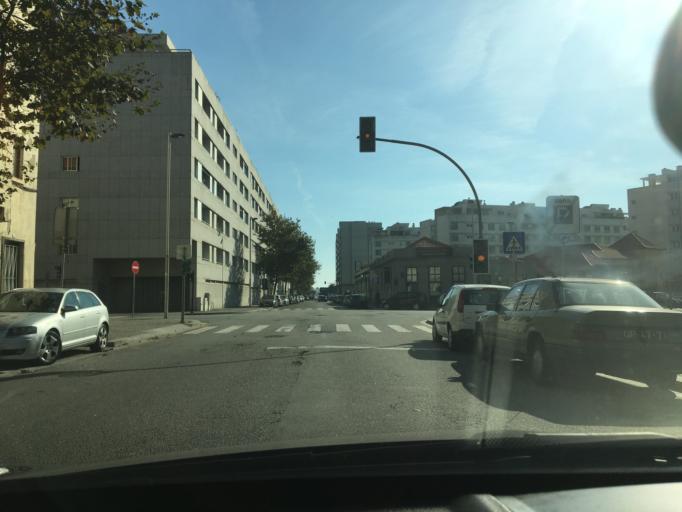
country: PT
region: Porto
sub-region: Matosinhos
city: Matosinhos
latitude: 41.1787
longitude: -8.6903
